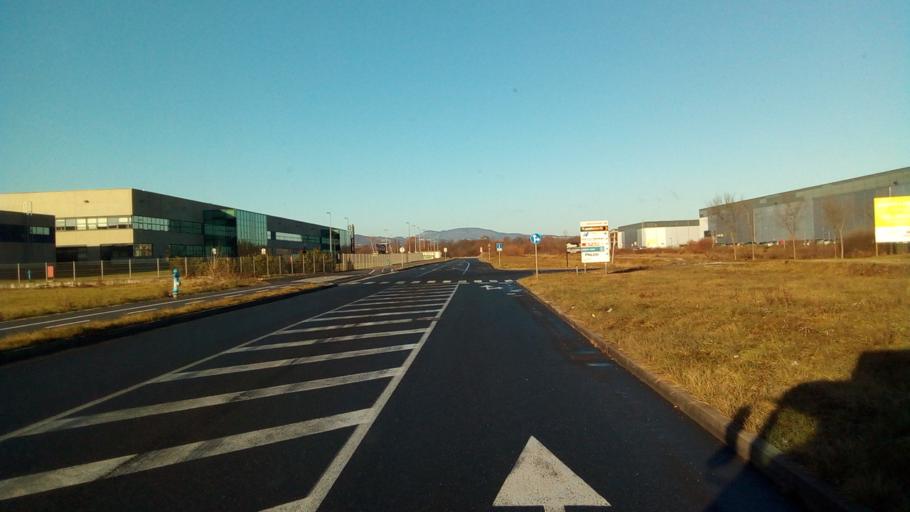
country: HR
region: Zagrebacka
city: Bestovje
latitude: 45.8016
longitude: 15.7733
